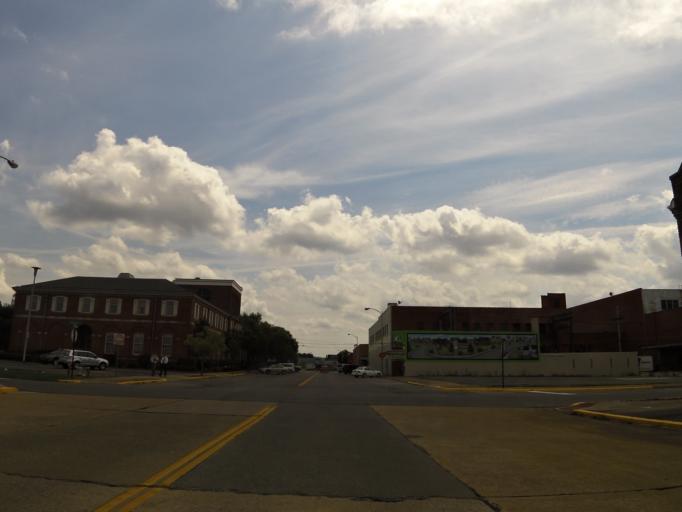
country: US
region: Tennessee
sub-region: Sullivan County
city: Kingsport
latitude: 36.5489
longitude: -82.5605
